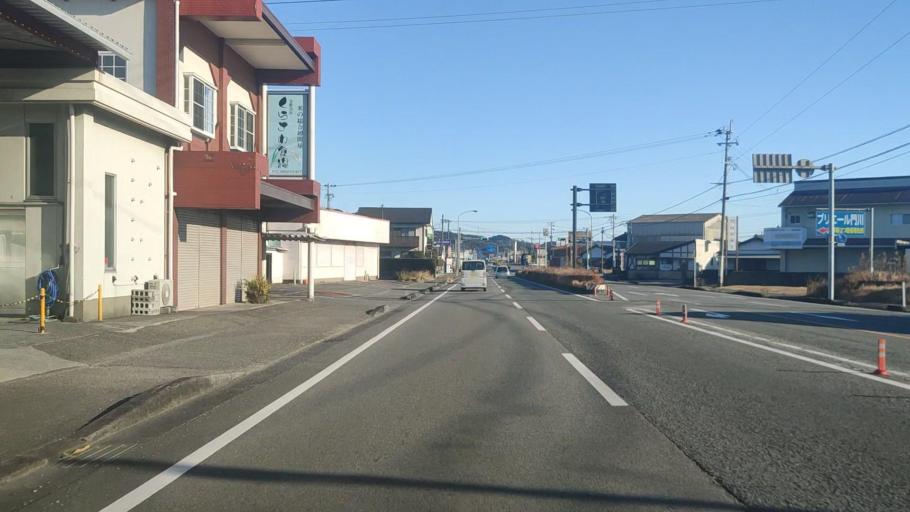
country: JP
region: Miyazaki
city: Nobeoka
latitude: 32.4747
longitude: 131.6529
